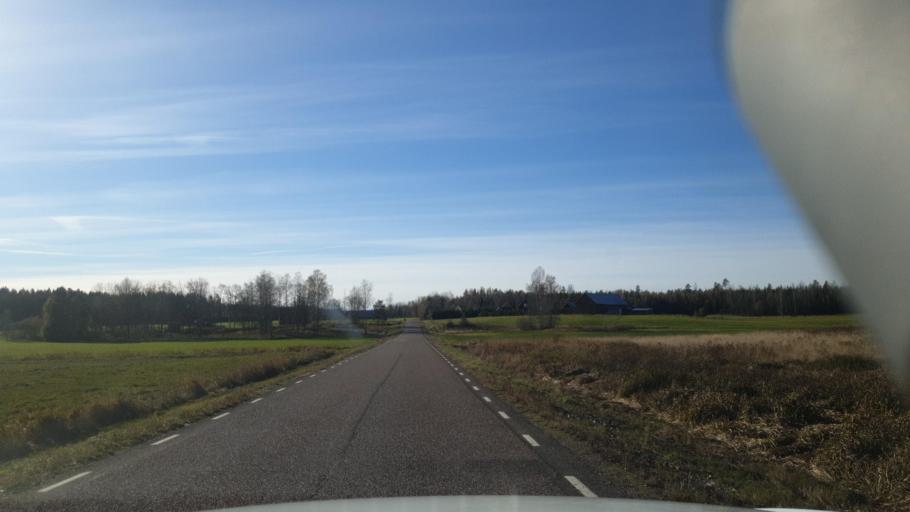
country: SE
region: Vaermland
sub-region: Karlstads Kommun
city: Edsvalla
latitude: 59.4911
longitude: 13.0979
